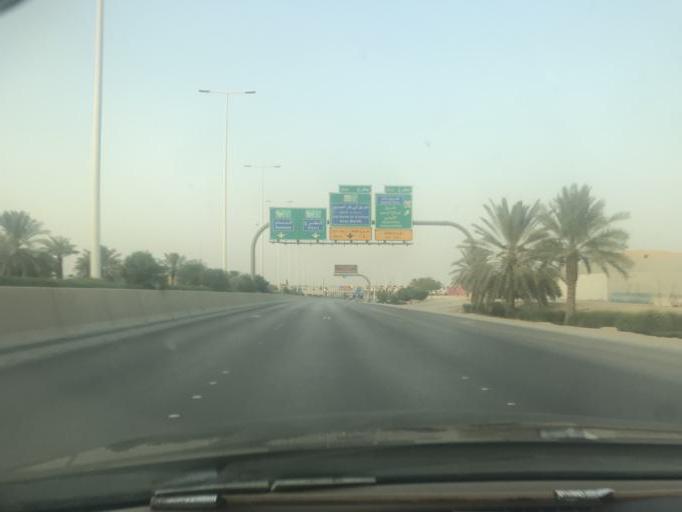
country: SA
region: Ar Riyad
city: Riyadh
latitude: 24.7208
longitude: 46.6880
